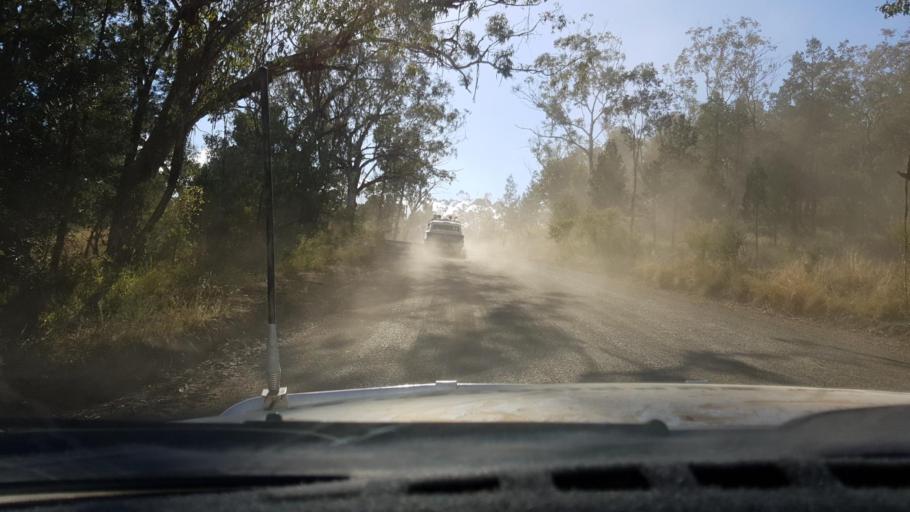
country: AU
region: New South Wales
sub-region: Tamworth Municipality
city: Manilla
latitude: -30.6539
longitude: 150.4915
